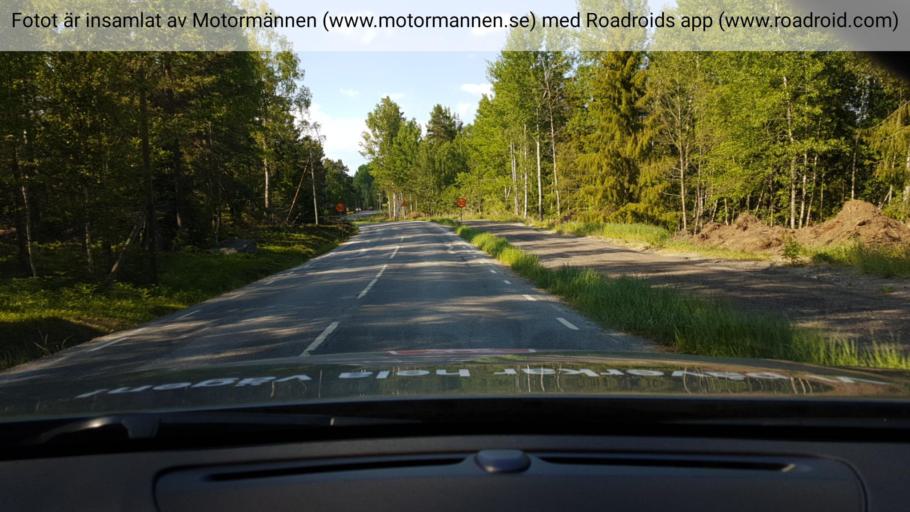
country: SE
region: Stockholm
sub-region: Varmdo Kommun
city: Mortnas
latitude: 59.2715
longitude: 18.4258
